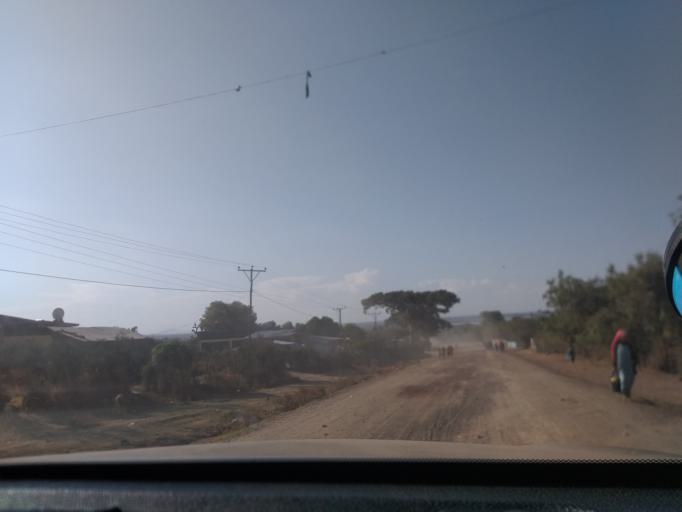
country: ET
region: Oromiya
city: Shashemene
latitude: 7.4856
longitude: 38.7494
